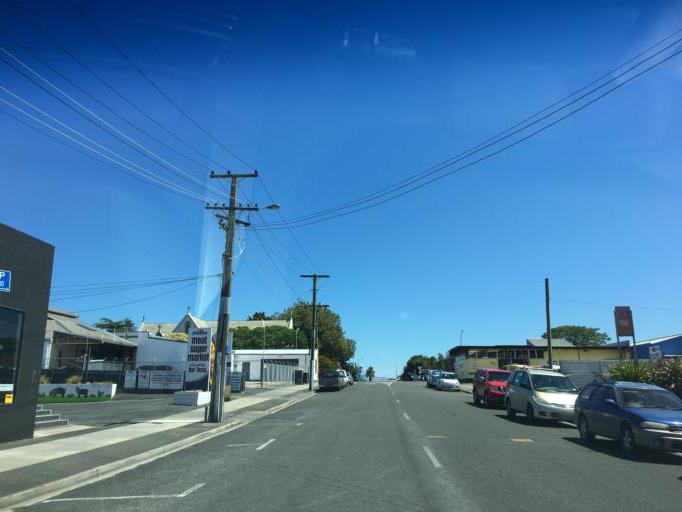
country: NZ
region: Gisborne
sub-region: Gisborne District
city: Gisborne
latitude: -38.6623
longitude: 178.0250
